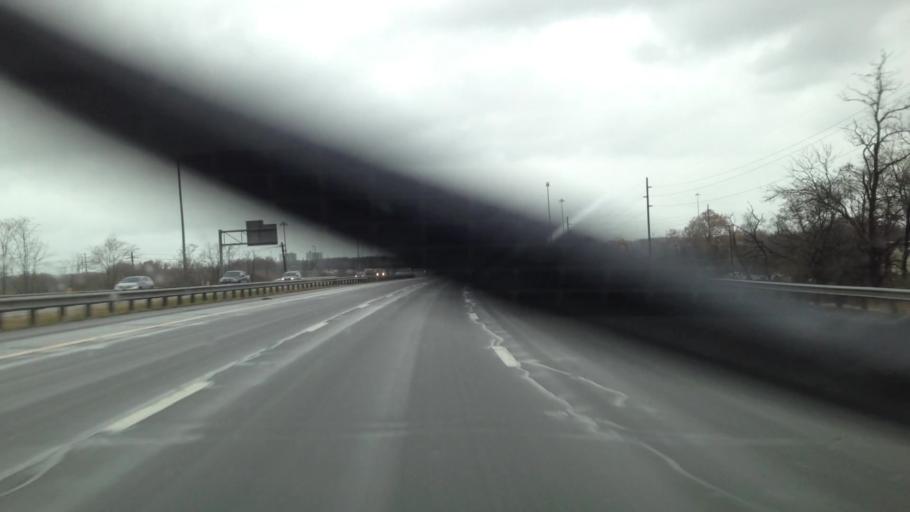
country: US
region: Ohio
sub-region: Lake County
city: Wickliffe
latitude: 41.5946
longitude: -81.4873
